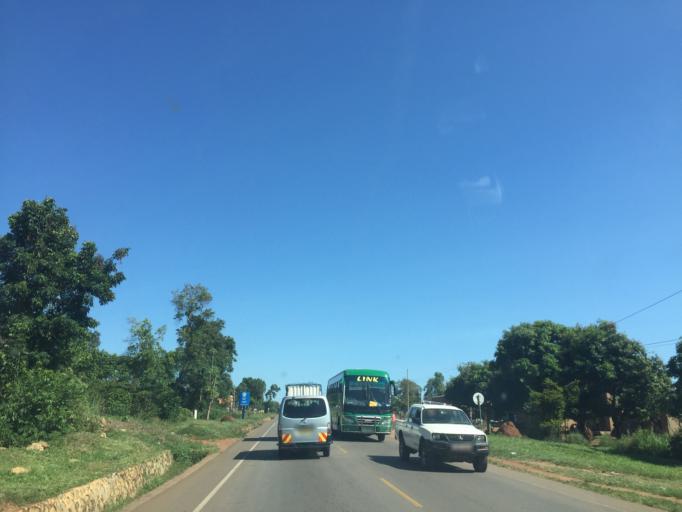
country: UG
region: Central Region
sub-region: Luwero District
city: Luwero
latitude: 0.8095
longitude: 32.5053
